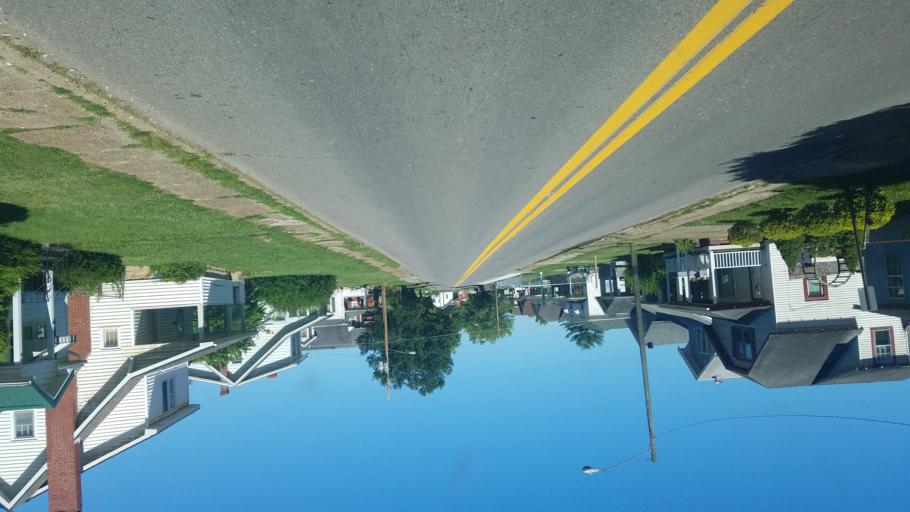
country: US
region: West Virginia
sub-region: Cabell County
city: Pea Ridge
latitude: 38.4301
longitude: -82.3776
